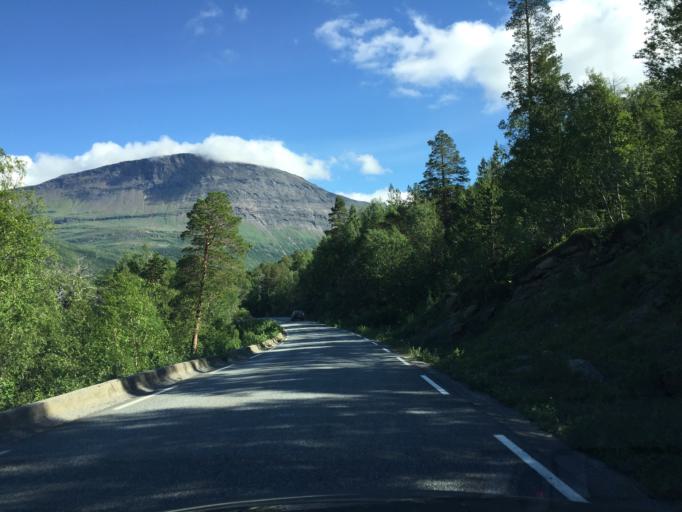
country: NO
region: Nordland
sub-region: Saltdal
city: Rognan
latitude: 66.8157
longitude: 15.4562
